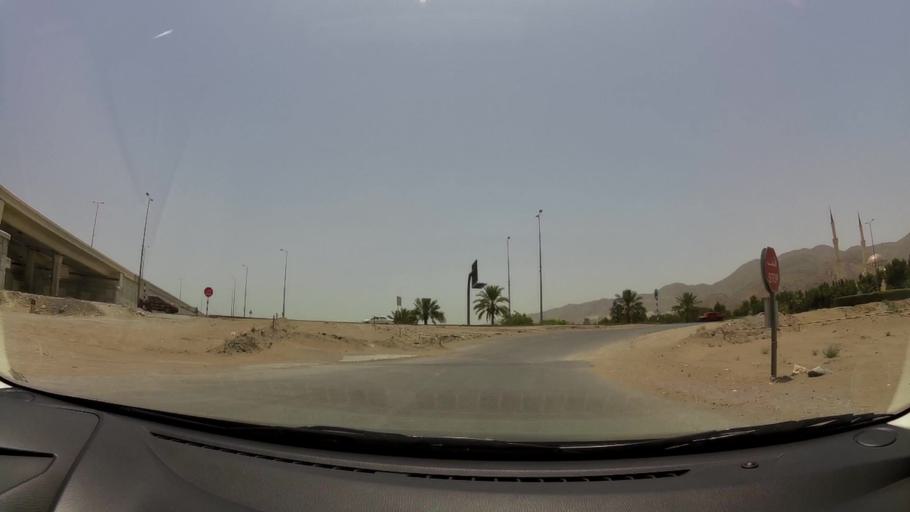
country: OM
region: Muhafazat Masqat
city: Bawshar
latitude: 23.5860
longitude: 58.4294
